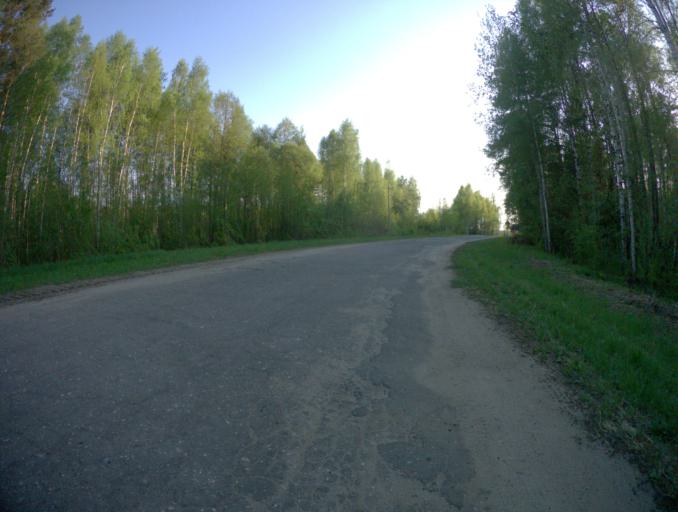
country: RU
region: Vladimir
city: Vyazniki
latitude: 56.3276
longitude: 42.1230
